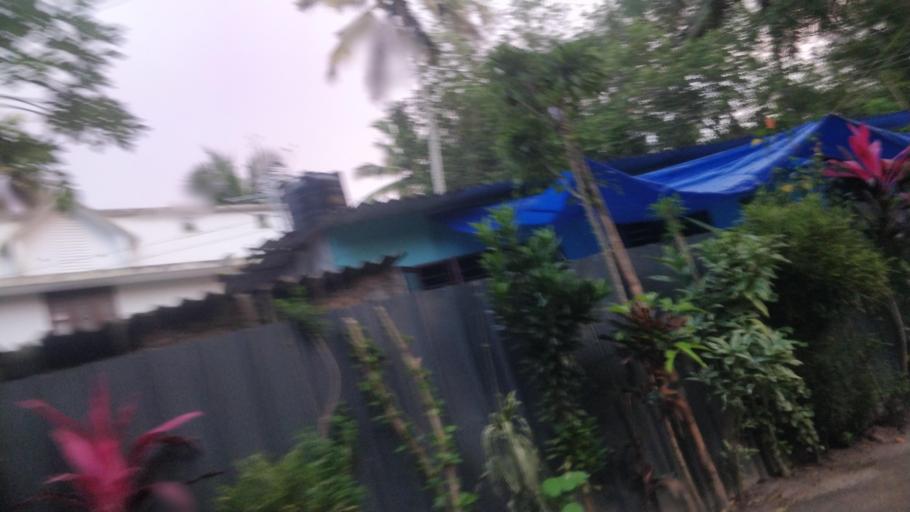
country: IN
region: Kerala
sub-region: Alappuzha
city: Shertallai
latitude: 9.6757
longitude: 76.3349
